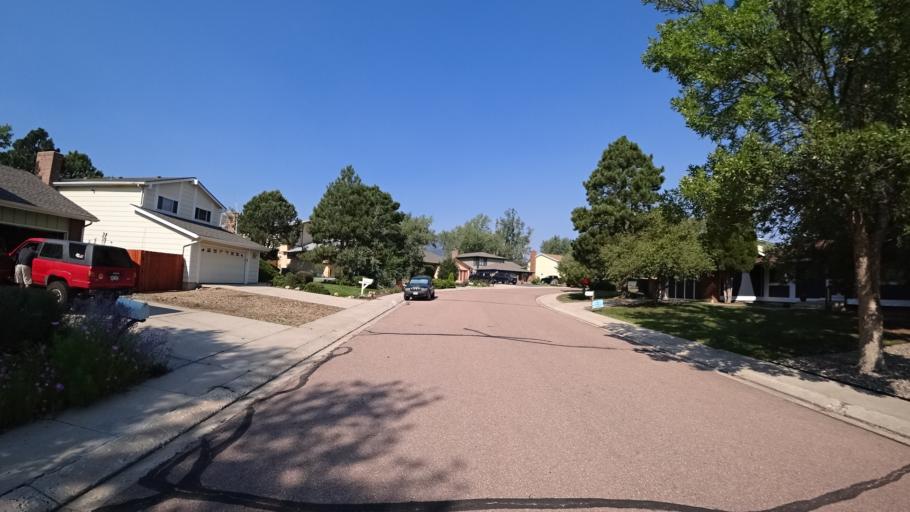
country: US
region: Colorado
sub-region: El Paso County
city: Stratmoor
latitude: 38.7859
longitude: -104.8190
